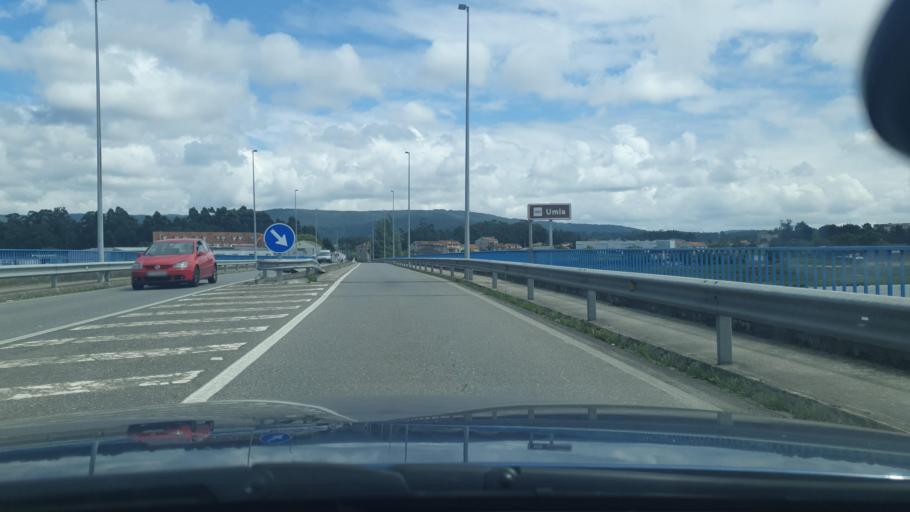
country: ES
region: Galicia
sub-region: Provincia de Pontevedra
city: Cambados
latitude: 42.5019
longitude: -8.8064
